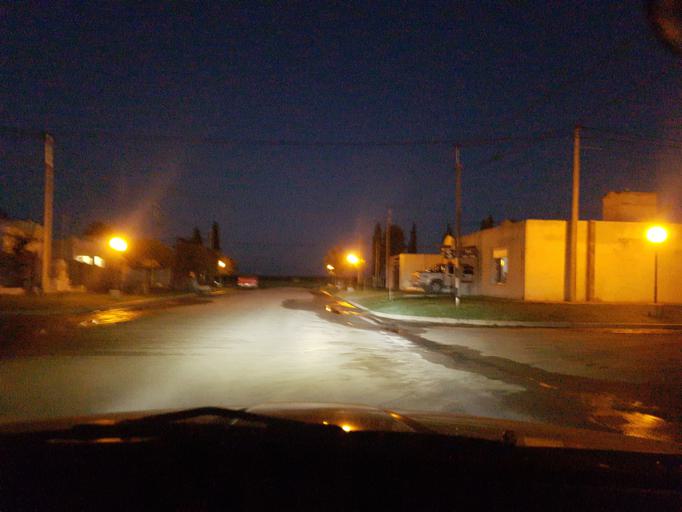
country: AR
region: Cordoba
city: Las Perdices
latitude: -32.7583
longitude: -63.7737
